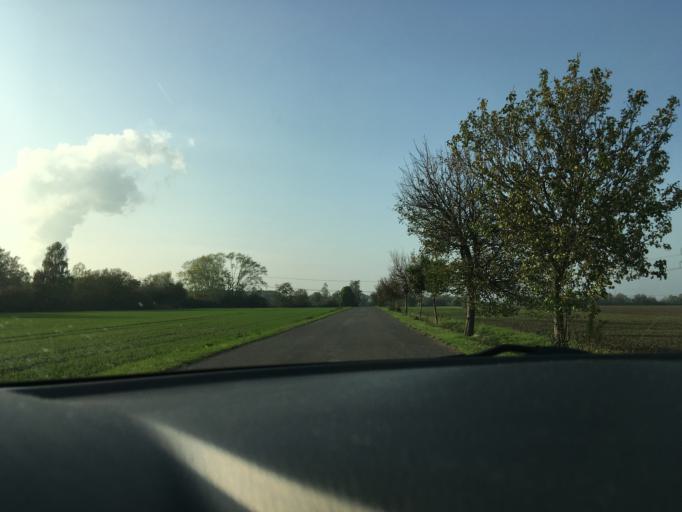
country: DE
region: Saxony
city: Neukieritzsch
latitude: 51.1843
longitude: 12.4339
